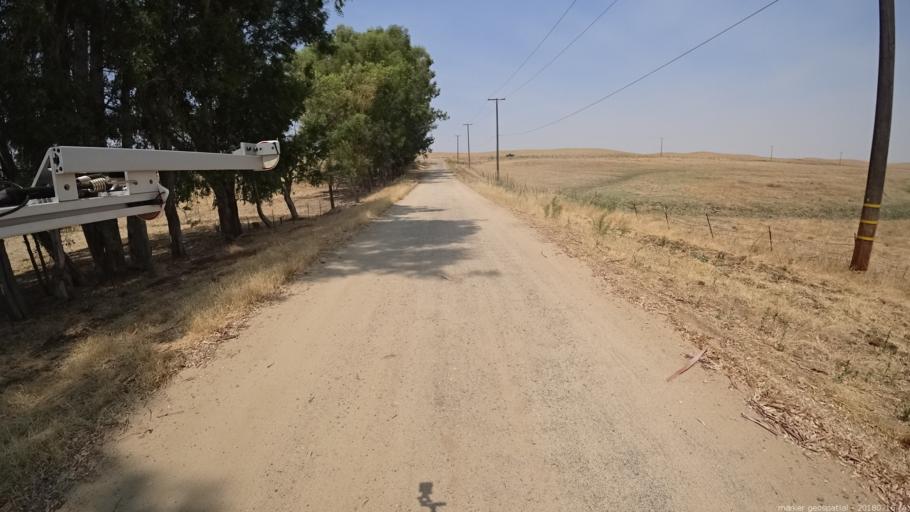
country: US
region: California
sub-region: Madera County
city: Bonadelle Ranchos-Madera Ranchos
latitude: 37.1033
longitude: -119.9391
